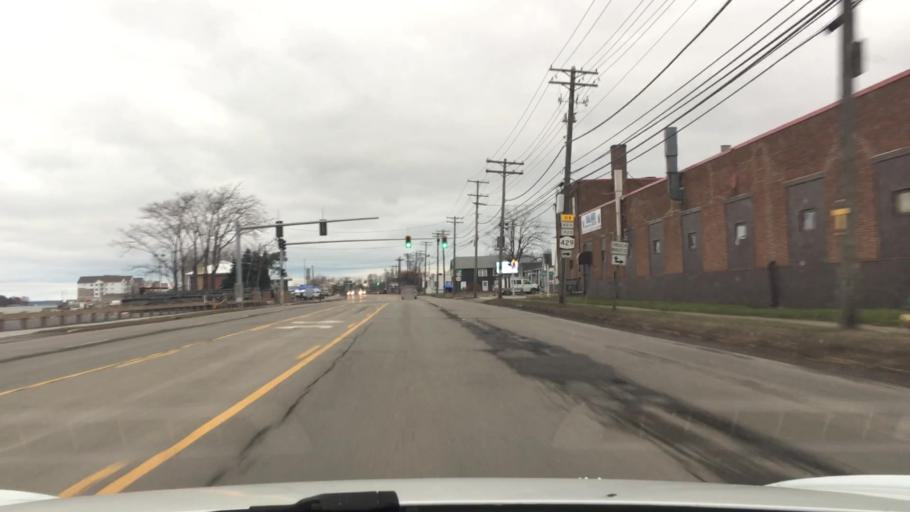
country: US
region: New York
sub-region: Erie County
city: Tonawanda
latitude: 43.0307
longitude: -78.8808
